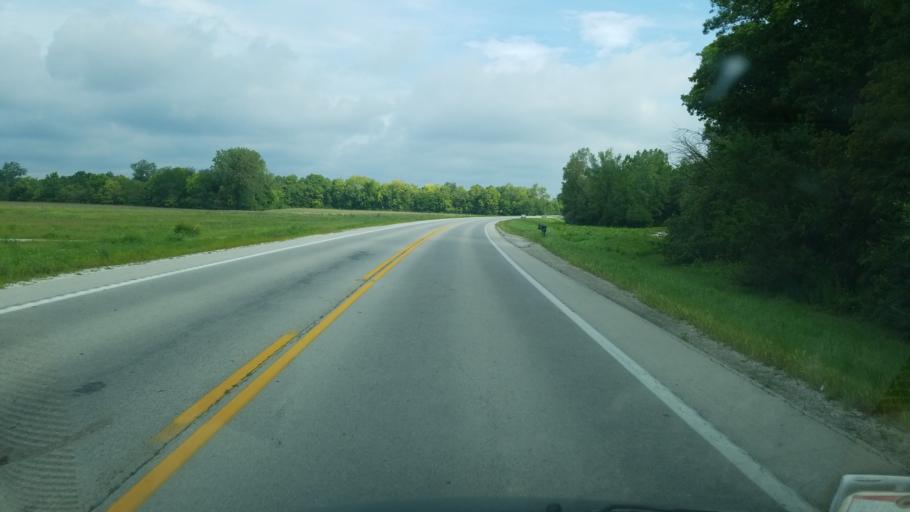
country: US
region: Ohio
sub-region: Sandusky County
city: Ballville
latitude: 41.2857
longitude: -83.1712
